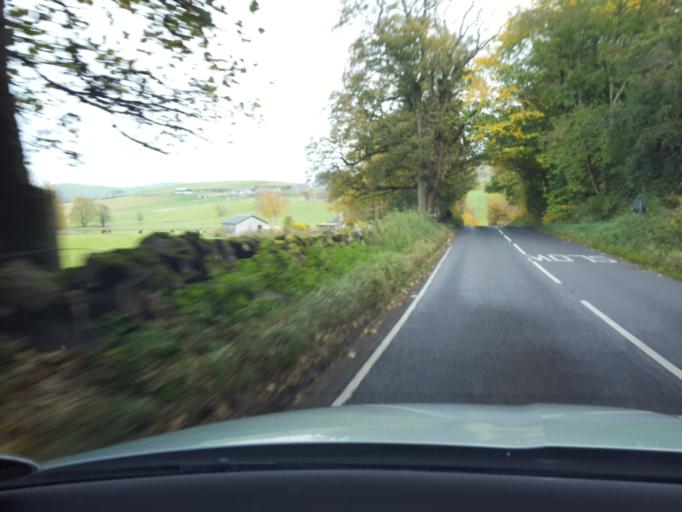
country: GB
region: Scotland
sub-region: The Scottish Borders
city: West Linton
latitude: 55.6849
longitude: -3.4096
